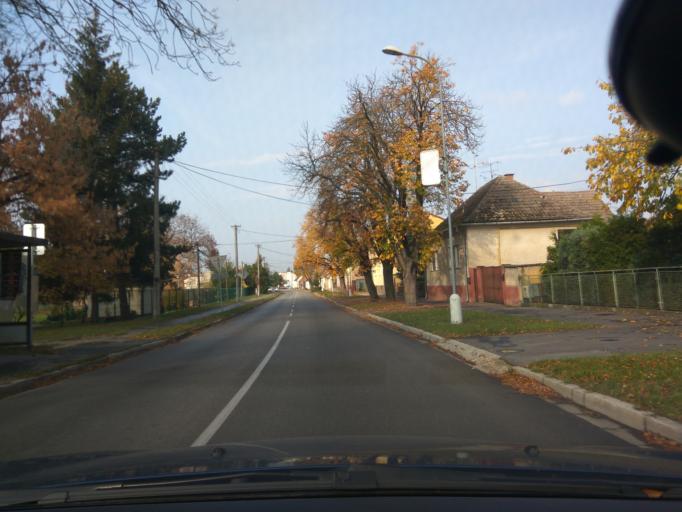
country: SK
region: Trnavsky
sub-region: Okres Trnava
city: Piestany
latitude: 48.6033
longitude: 17.8295
